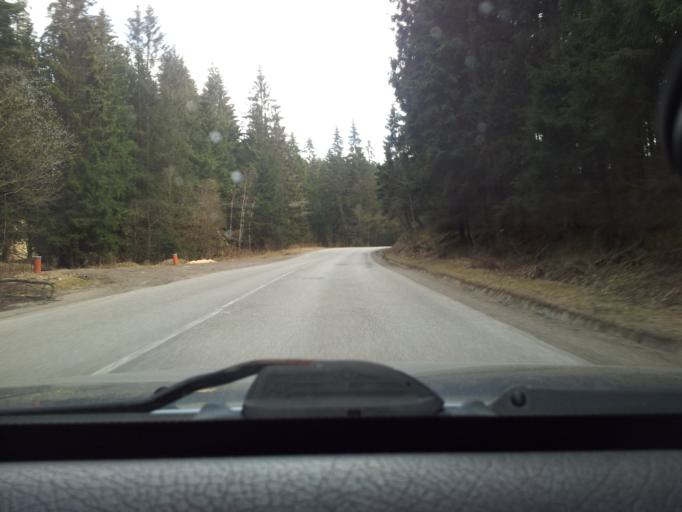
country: SK
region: Banskobystricky
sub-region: Okres Ziar nad Hronom
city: Kremnica
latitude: 48.7528
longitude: 18.8996
